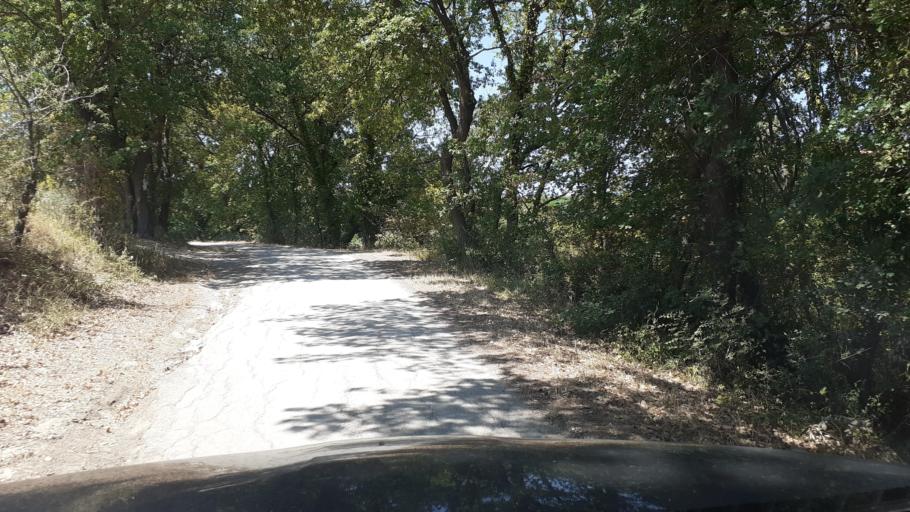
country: IT
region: Abruzzo
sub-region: Provincia di Chieti
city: Santa Maria Imbaro
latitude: 42.2099
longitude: 14.4747
